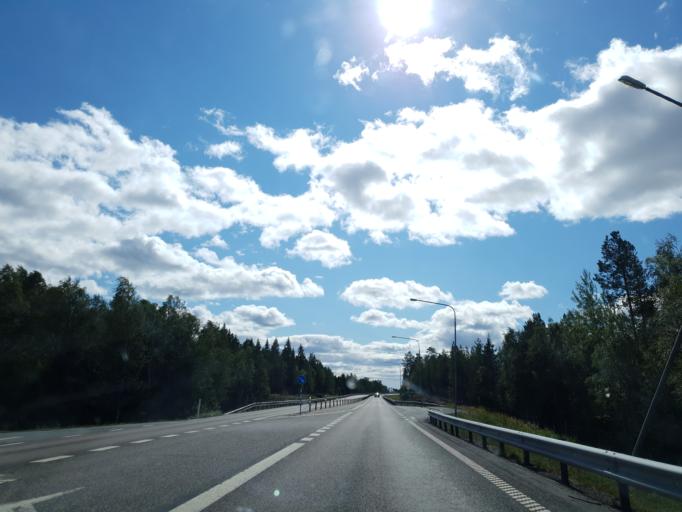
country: SE
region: Vaesternorrland
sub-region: OErnskoeldsviks Kommun
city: Husum
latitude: 63.3752
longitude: 19.1902
